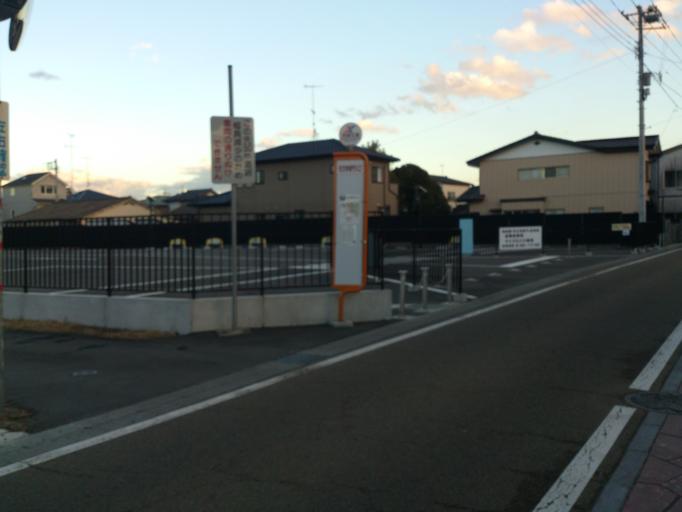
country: JP
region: Ibaraki
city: Mito-shi
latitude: 36.3780
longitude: 140.4532
